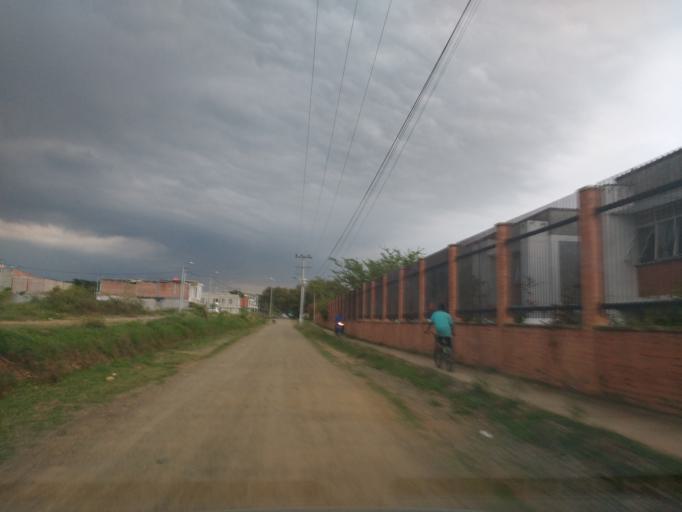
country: CO
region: Cauca
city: Santander de Quilichao
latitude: 3.0072
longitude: -76.4756
